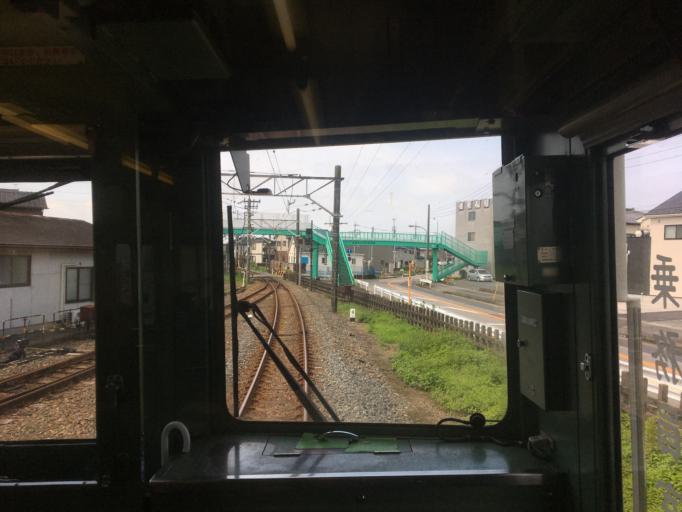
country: JP
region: Tochigi
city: Sano
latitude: 36.3052
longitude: 139.5741
